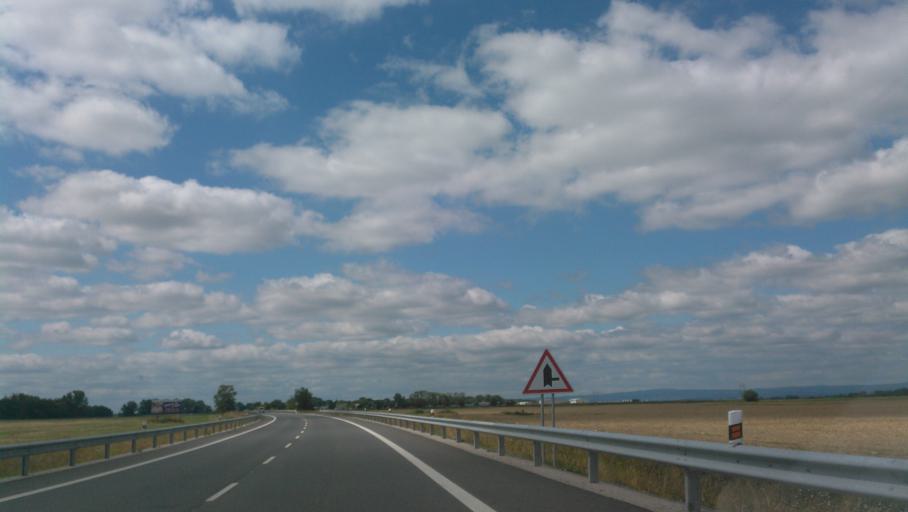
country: SK
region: Trnavsky
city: Sladkovicovo
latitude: 48.2022
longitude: 17.5479
